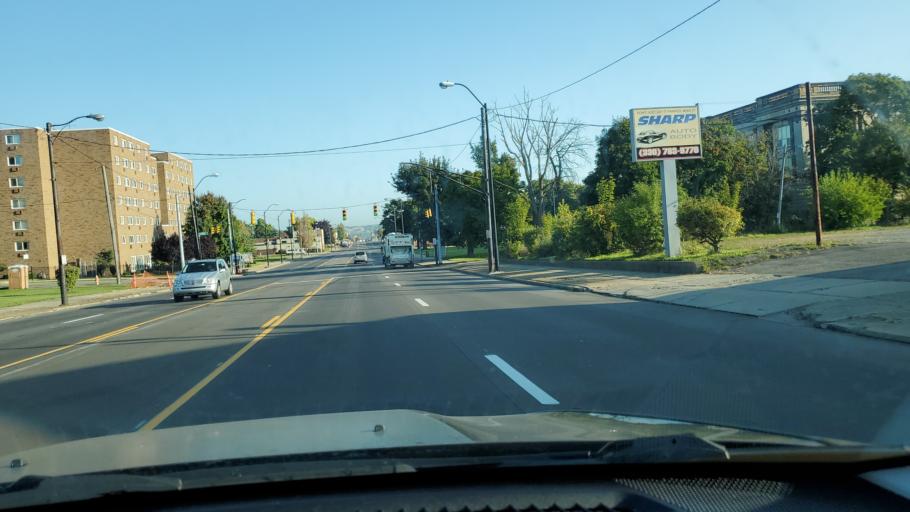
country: US
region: Ohio
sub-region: Mahoning County
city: Youngstown
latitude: 41.0805
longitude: -80.6569
